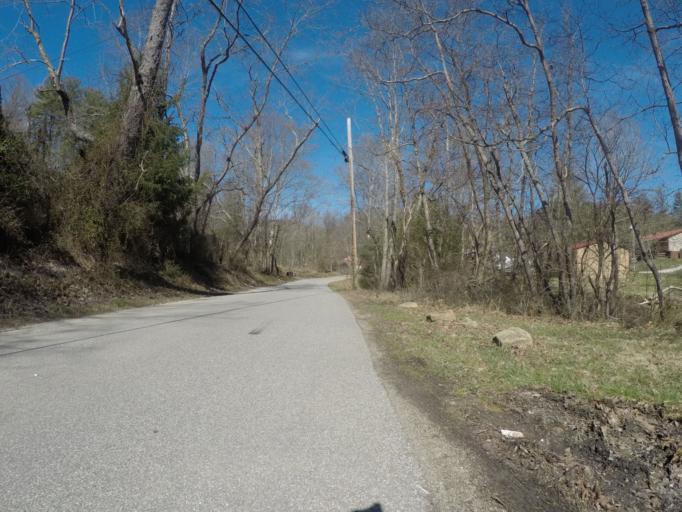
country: US
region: Ohio
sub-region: Lawrence County
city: Burlington
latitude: 38.4547
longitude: -82.5025
